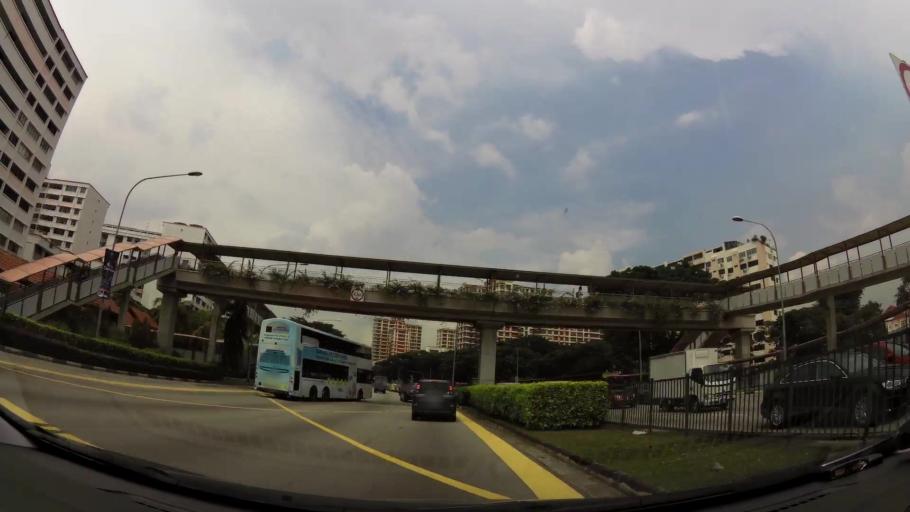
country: SG
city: Singapore
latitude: 1.3283
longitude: 103.9055
